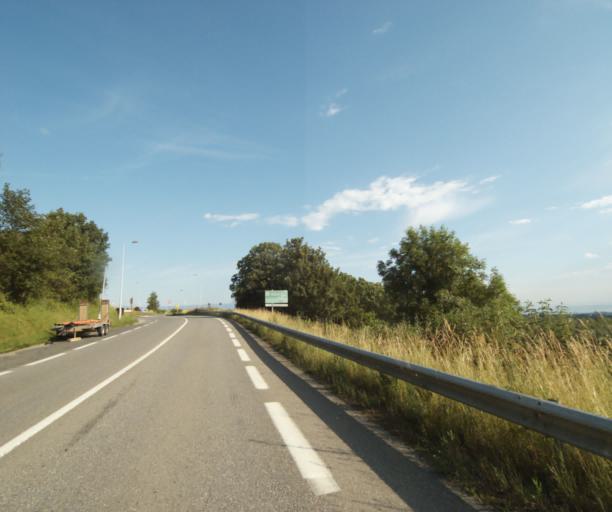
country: FR
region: Rhone-Alpes
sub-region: Departement de la Haute-Savoie
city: Thonon-les-Bains
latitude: 46.3672
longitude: 6.5037
